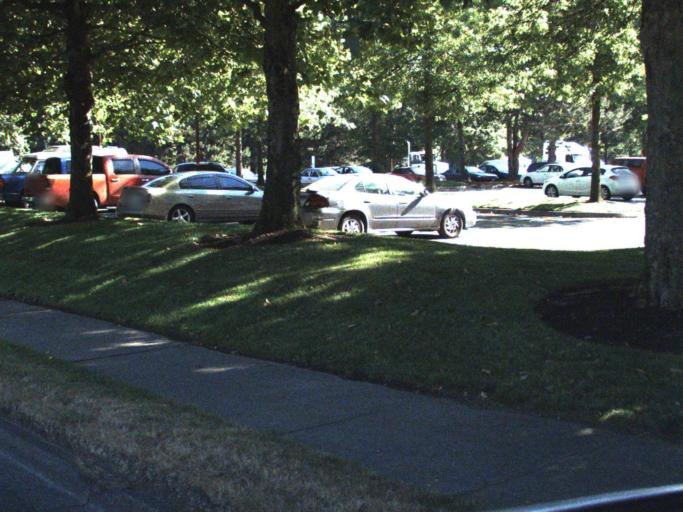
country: US
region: Washington
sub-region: King County
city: Kent
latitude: 47.4152
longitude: -122.2494
